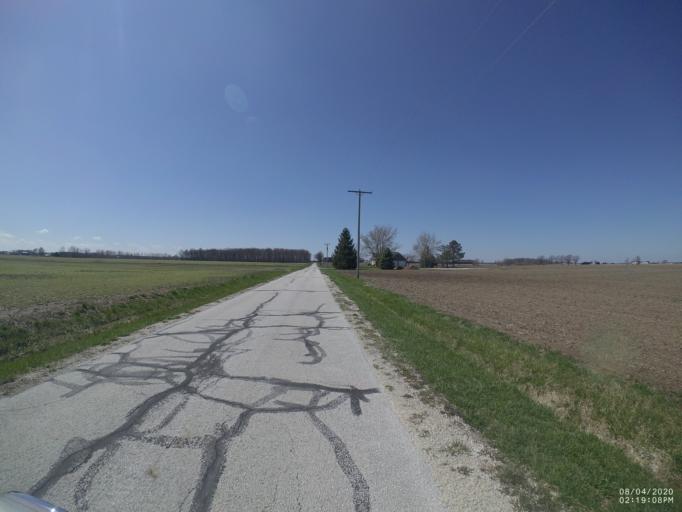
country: US
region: Ohio
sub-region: Sandusky County
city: Stony Prairie
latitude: 41.2894
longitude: -83.2382
